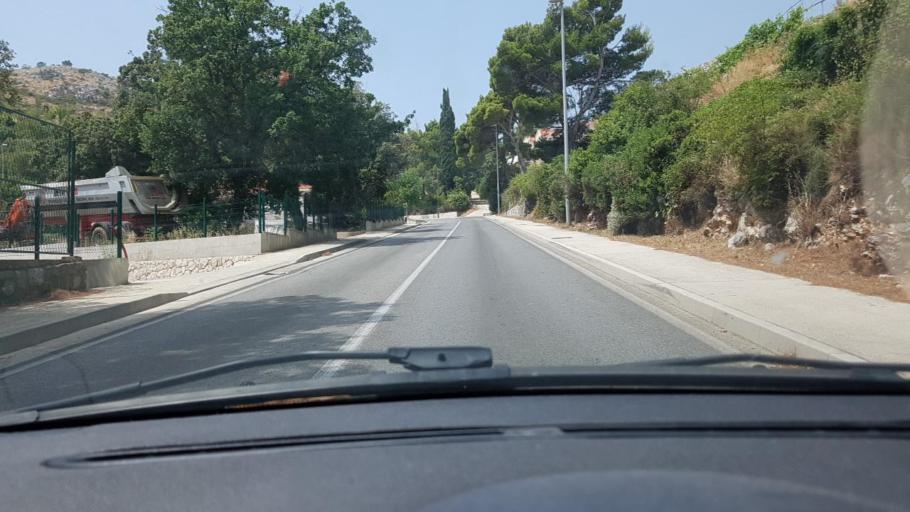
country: HR
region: Dubrovacko-Neretvanska
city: Cibaca
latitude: 42.6304
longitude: 18.1588
